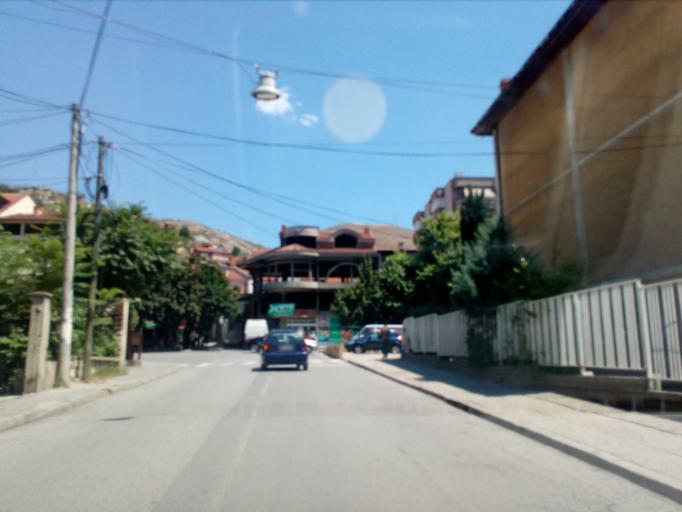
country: MK
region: Veles
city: Veles
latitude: 41.7138
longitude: 21.7863
